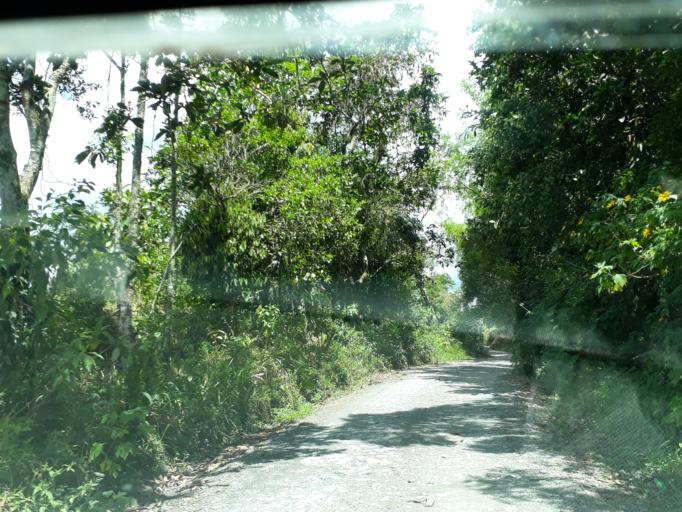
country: CO
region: Cundinamarca
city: Topaipi
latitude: 5.3644
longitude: -74.1976
